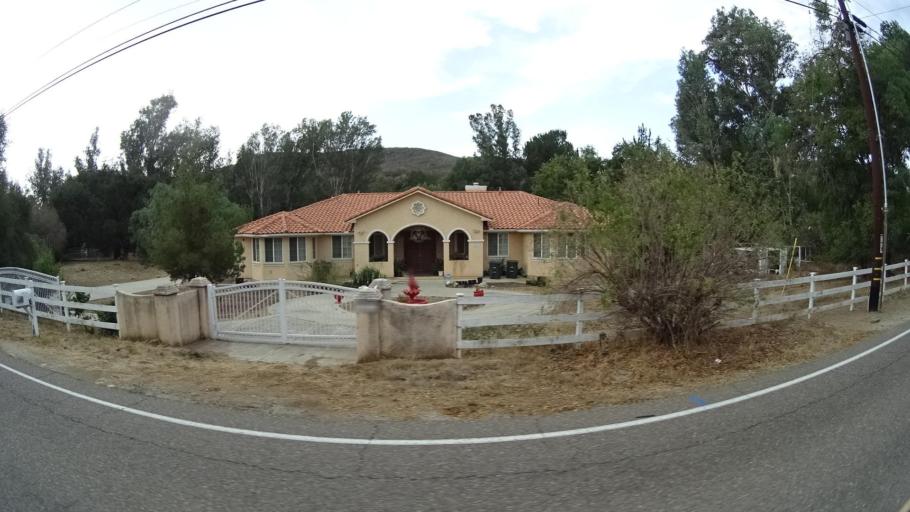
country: US
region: California
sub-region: San Diego County
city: Ramona
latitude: 32.9697
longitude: -116.9130
